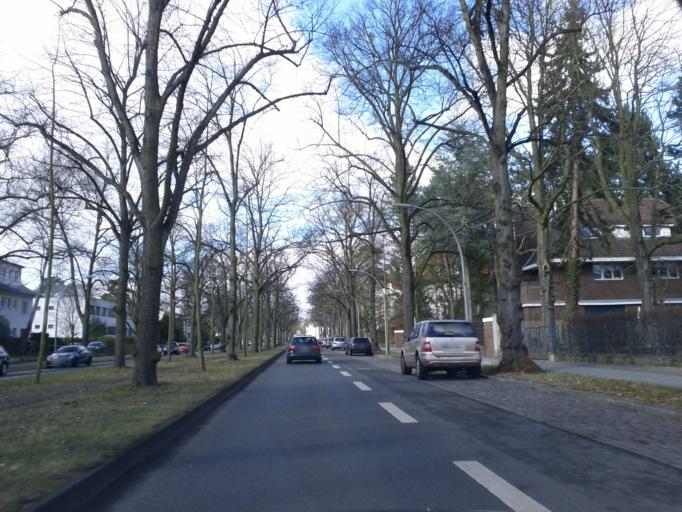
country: DE
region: Berlin
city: Schmargendorf
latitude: 52.4740
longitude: 13.2848
